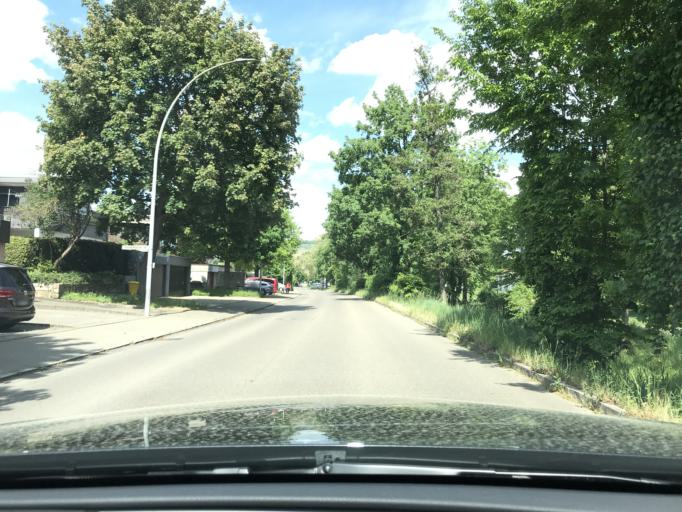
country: DE
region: Baden-Wuerttemberg
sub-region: Regierungsbezirk Stuttgart
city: Weinstadt-Endersbach
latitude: 48.8089
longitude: 9.3581
